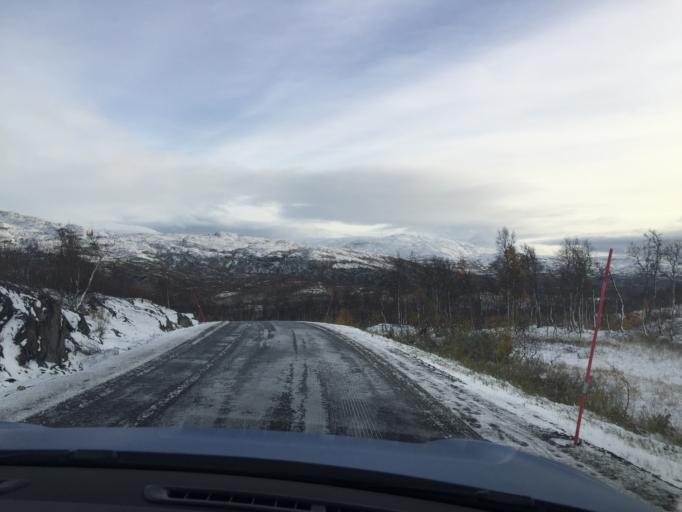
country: NO
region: Nordland
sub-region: Sorfold
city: Straumen
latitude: 67.0891
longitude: 16.0189
